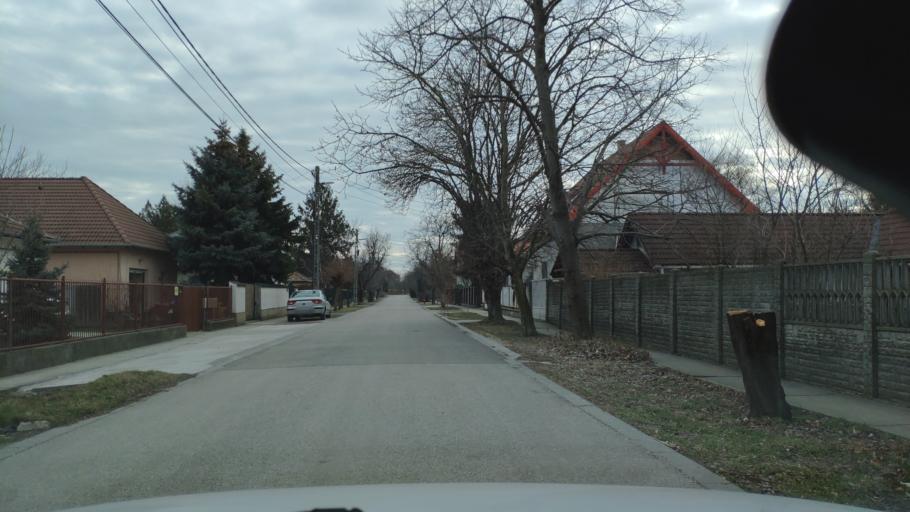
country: HU
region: Pest
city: Dunaharaszti
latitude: 47.3515
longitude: 19.0925
